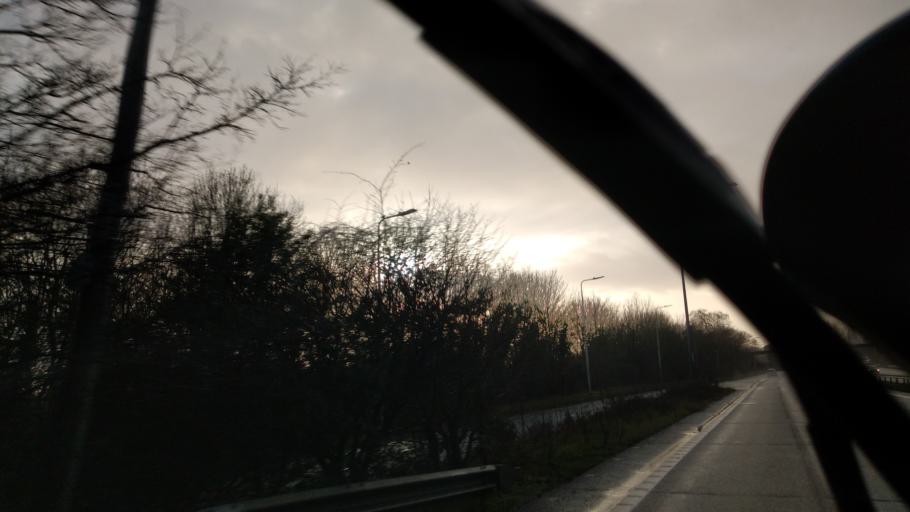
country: GB
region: England
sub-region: Hampshire
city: Havant
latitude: 50.8482
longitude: -0.9667
